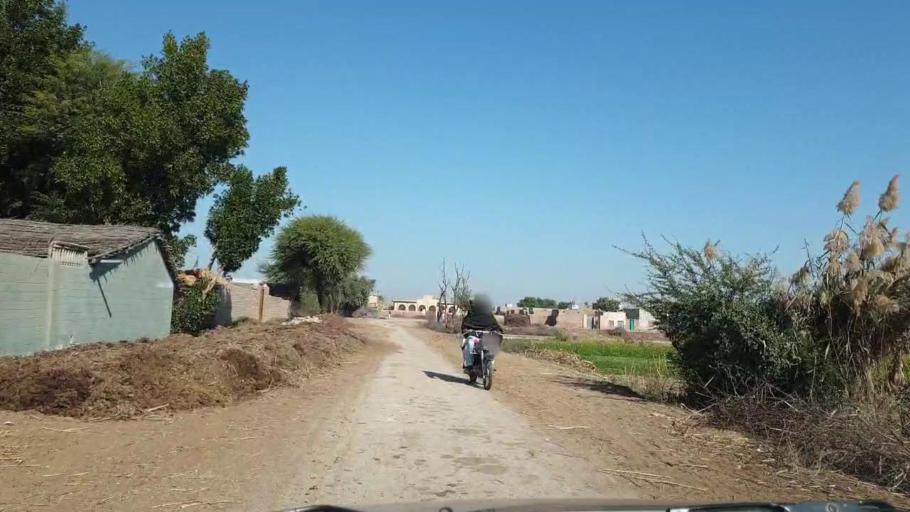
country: PK
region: Sindh
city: Sinjhoro
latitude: 26.1088
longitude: 68.8426
